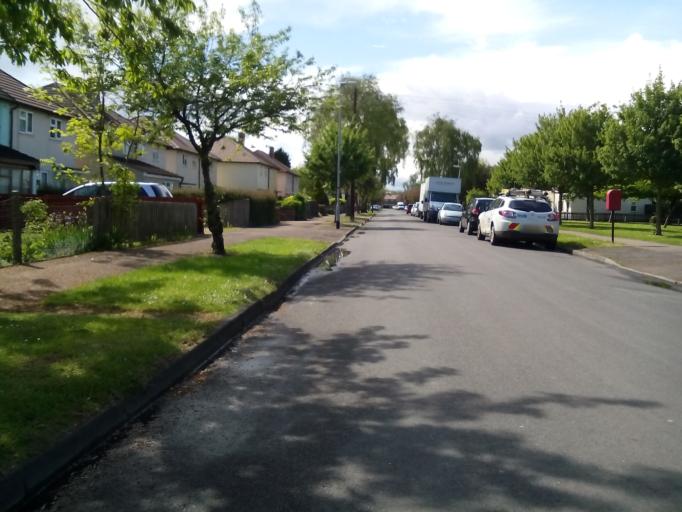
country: GB
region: England
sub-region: Cambridgeshire
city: Cambridge
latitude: 52.1838
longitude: 0.1583
